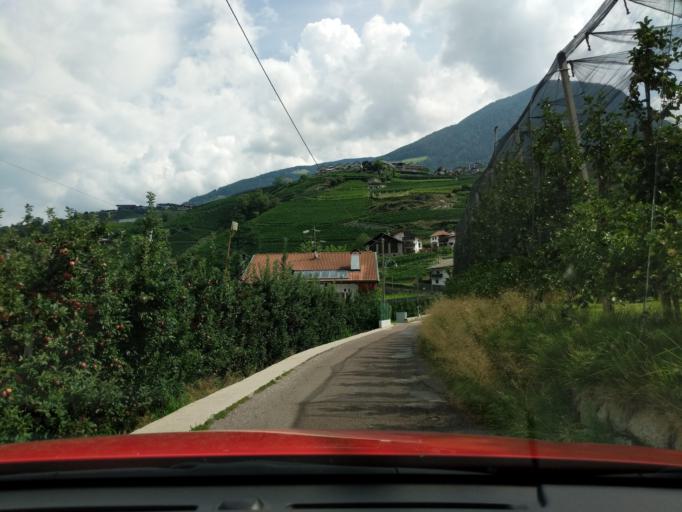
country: IT
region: Trentino-Alto Adige
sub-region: Bolzano
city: Scena
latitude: 46.6774
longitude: 11.1813
